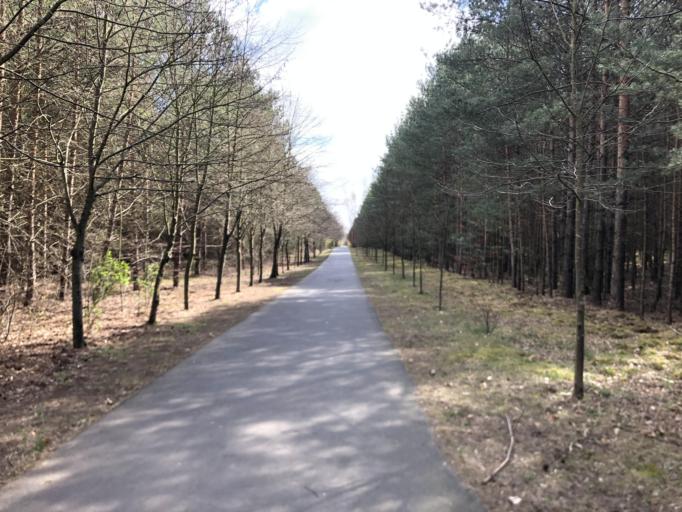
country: DE
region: Brandenburg
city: Hohen Neuendorf
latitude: 52.6600
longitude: 13.2950
